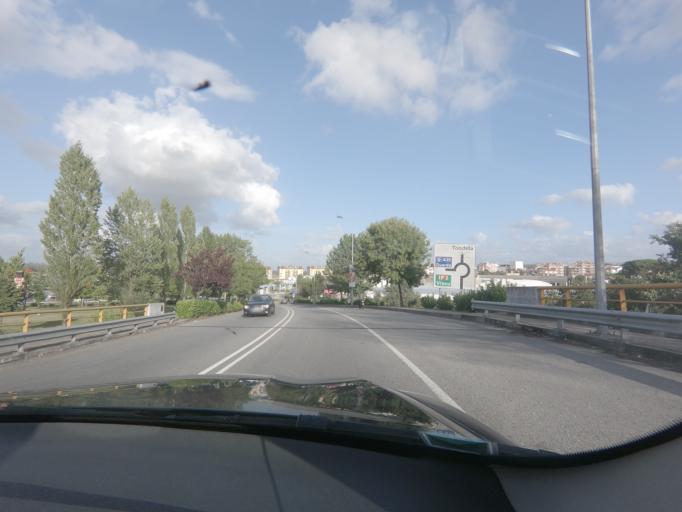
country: PT
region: Viseu
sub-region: Concelho de Tondela
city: Tondela
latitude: 40.5258
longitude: -8.0880
